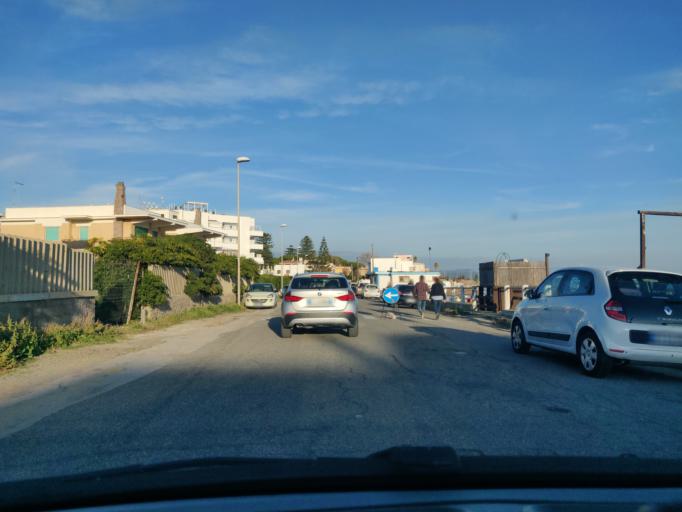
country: IT
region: Latium
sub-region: Citta metropolitana di Roma Capitale
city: Santa Marinella
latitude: 42.0301
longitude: 11.8406
